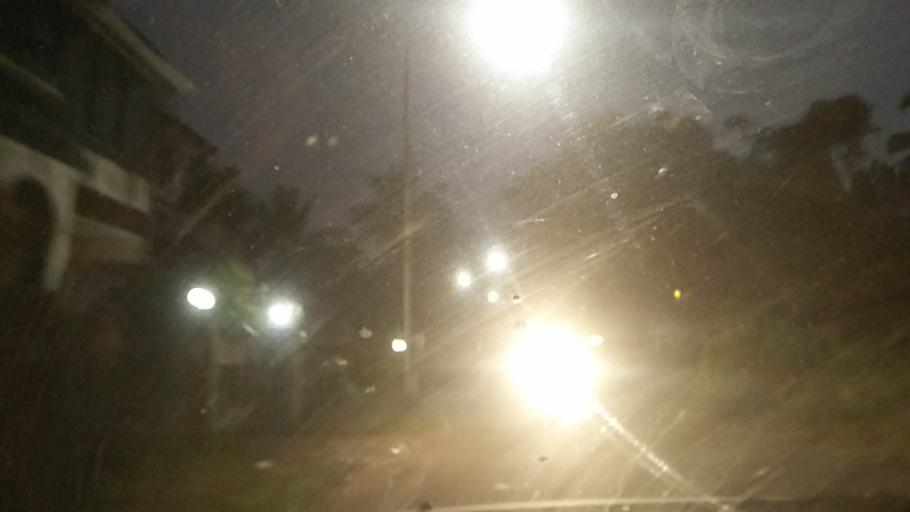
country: IN
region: Goa
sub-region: South Goa
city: Madgaon
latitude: 15.2633
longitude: 73.9648
